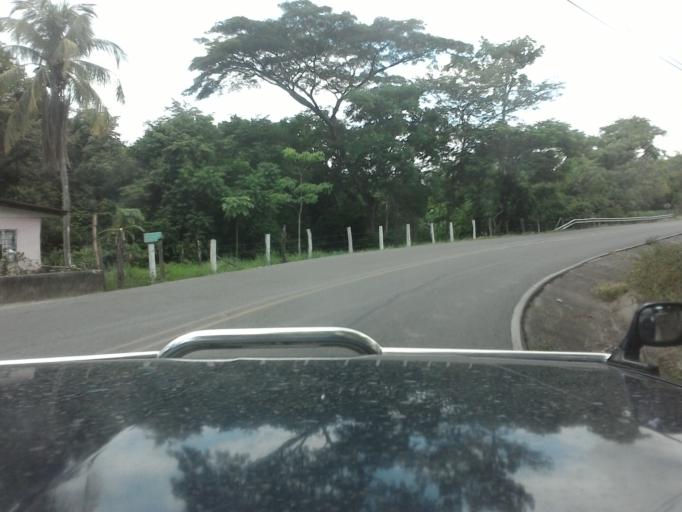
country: CR
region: Guanacaste
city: Juntas
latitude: 10.1900
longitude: -84.8423
